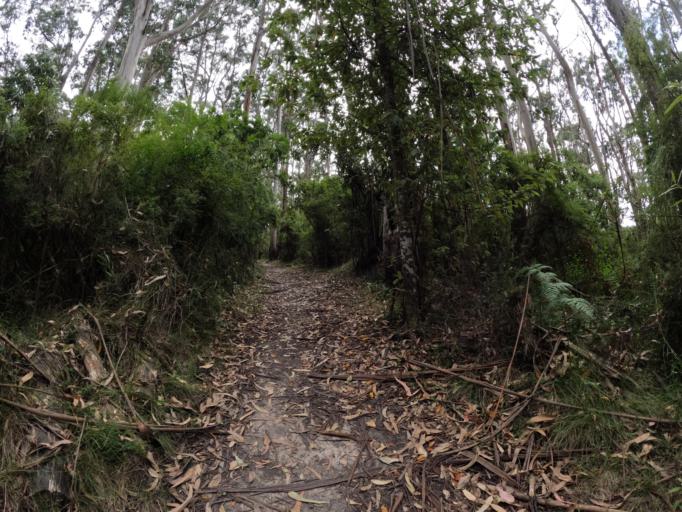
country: AU
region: Victoria
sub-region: Colac-Otway
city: Apollo Bay
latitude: -38.7919
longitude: 143.6158
